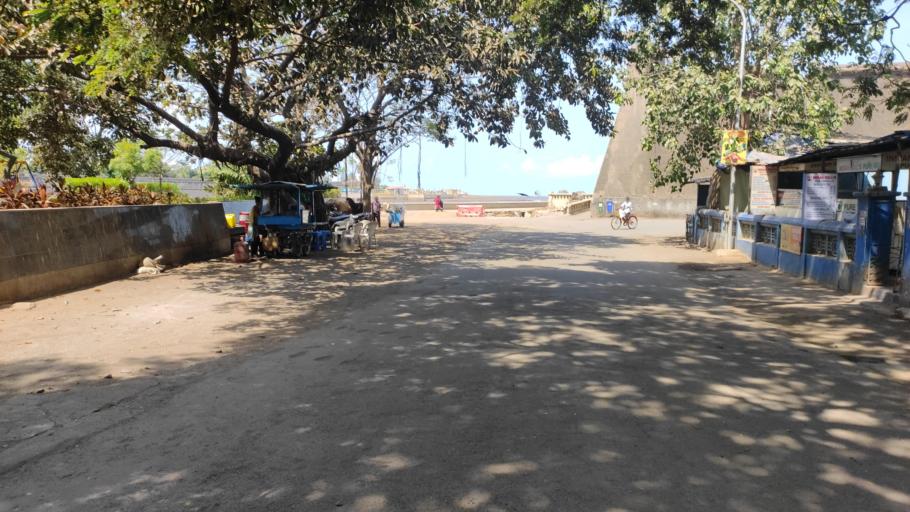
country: IN
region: Daman and Diu
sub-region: Daman District
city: Daman
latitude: 20.4134
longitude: 72.8334
